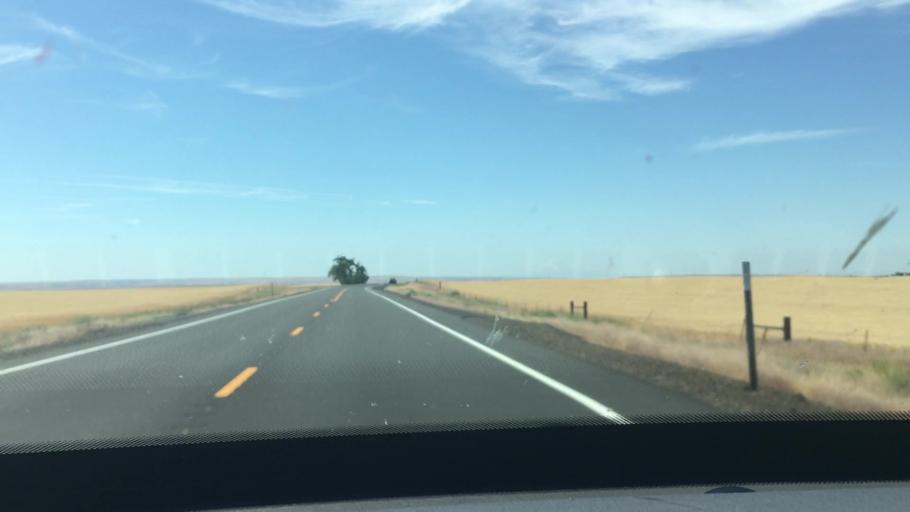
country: US
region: Oregon
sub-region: Sherman County
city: Moro
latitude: 45.3033
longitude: -120.7652
